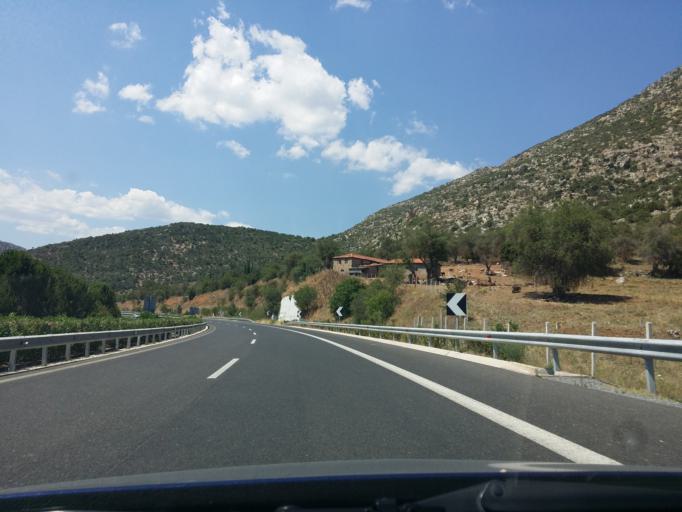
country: GR
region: Peloponnese
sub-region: Nomos Arkadias
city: Tripoli
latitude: 37.6304
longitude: 22.4681
